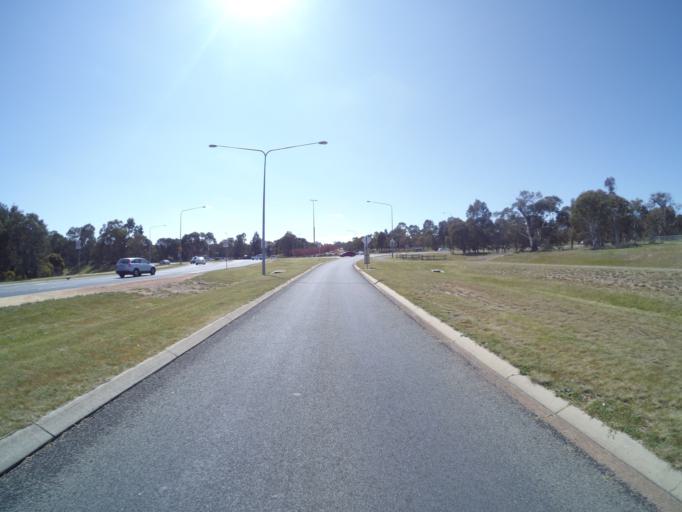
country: AU
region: Australian Capital Territory
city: Macarthur
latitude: -35.4383
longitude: 149.0906
